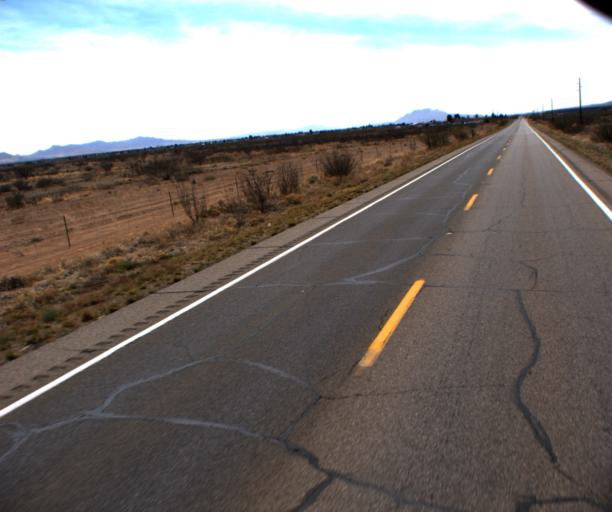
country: US
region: Arizona
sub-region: Cochise County
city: Pirtleville
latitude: 31.3780
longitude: -109.5793
